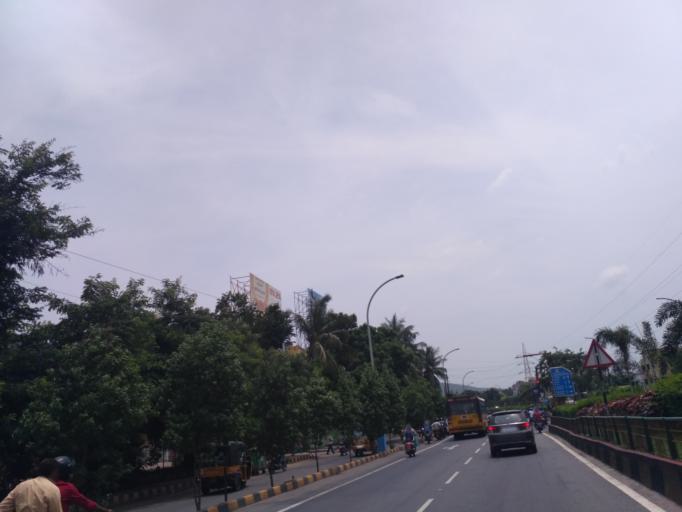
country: IN
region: Andhra Pradesh
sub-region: Vishakhapatnam
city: Yarada
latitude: 17.7348
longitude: 83.2867
